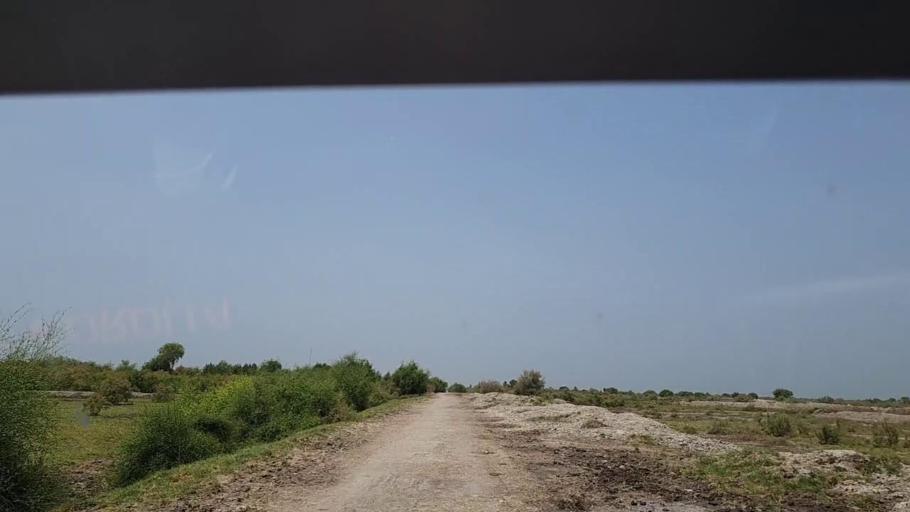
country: PK
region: Sindh
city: Adilpur
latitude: 27.8911
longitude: 69.2500
